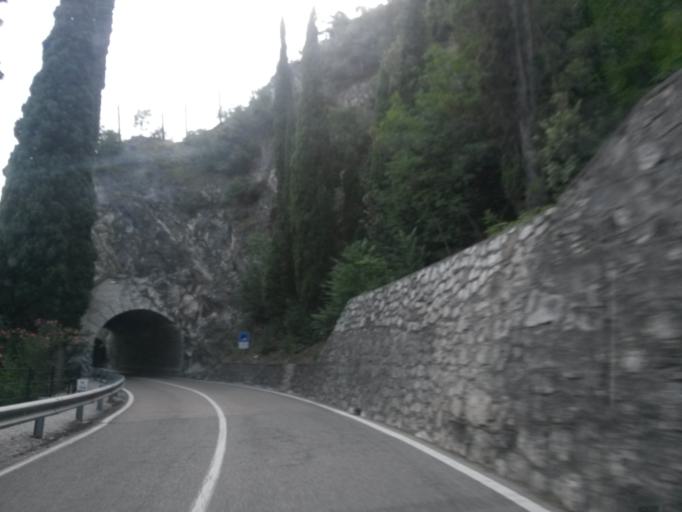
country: IT
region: Lombardy
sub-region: Provincia di Brescia
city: Limone sul Garda
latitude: 45.8242
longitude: 10.8092
